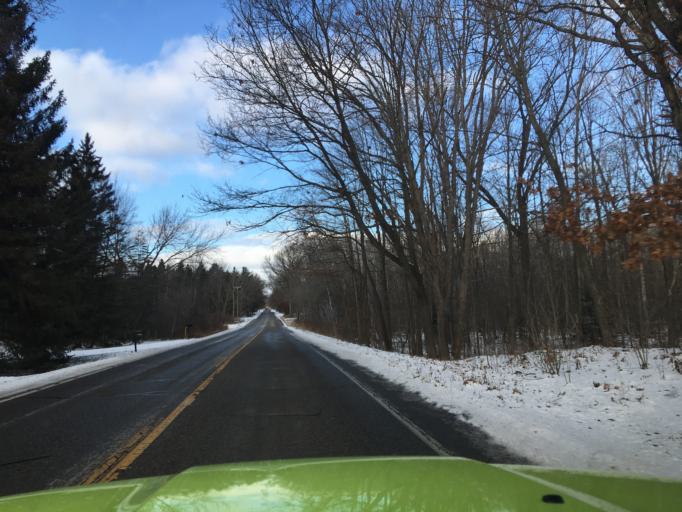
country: US
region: Michigan
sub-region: Montcalm County
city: Greenville
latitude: 43.1944
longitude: -85.2828
